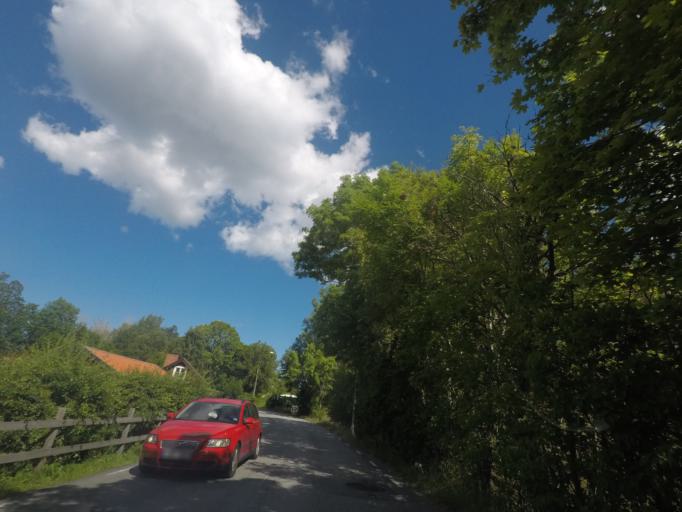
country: SE
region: Stockholm
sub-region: Norrtalje Kommun
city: Arno
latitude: 60.0967
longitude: 18.8115
